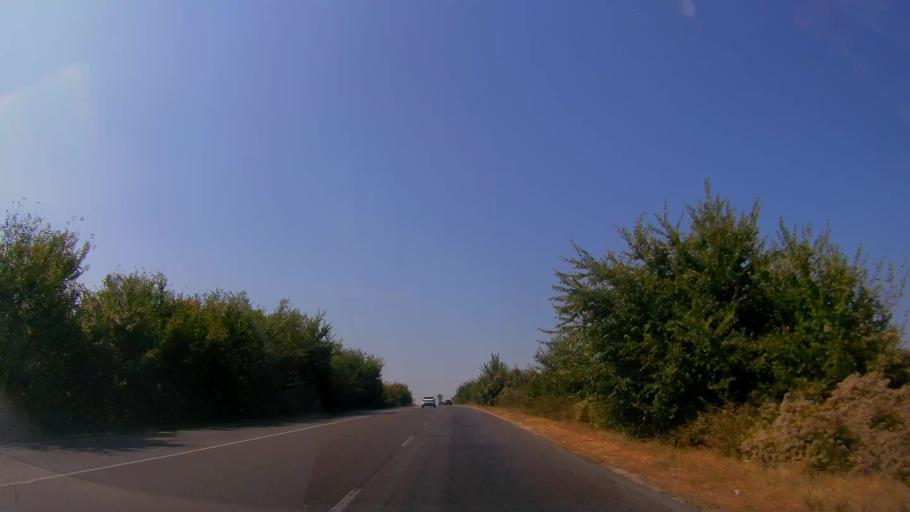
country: BG
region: Ruse
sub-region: Obshtina Vetovo
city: Senovo
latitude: 43.5617
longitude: 26.3638
